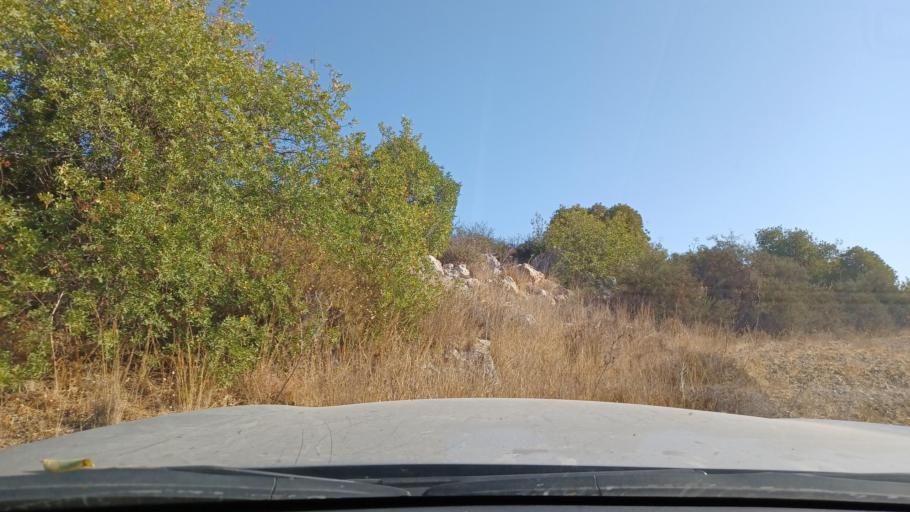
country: CY
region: Pafos
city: Polis
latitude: 35.0030
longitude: 32.4903
